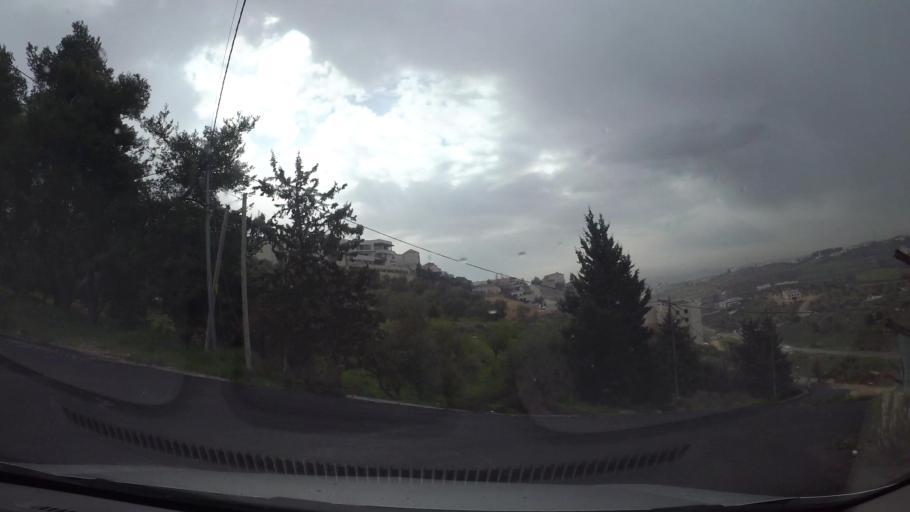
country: JO
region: Amman
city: Wadi as Sir
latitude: 31.9901
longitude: 35.8154
